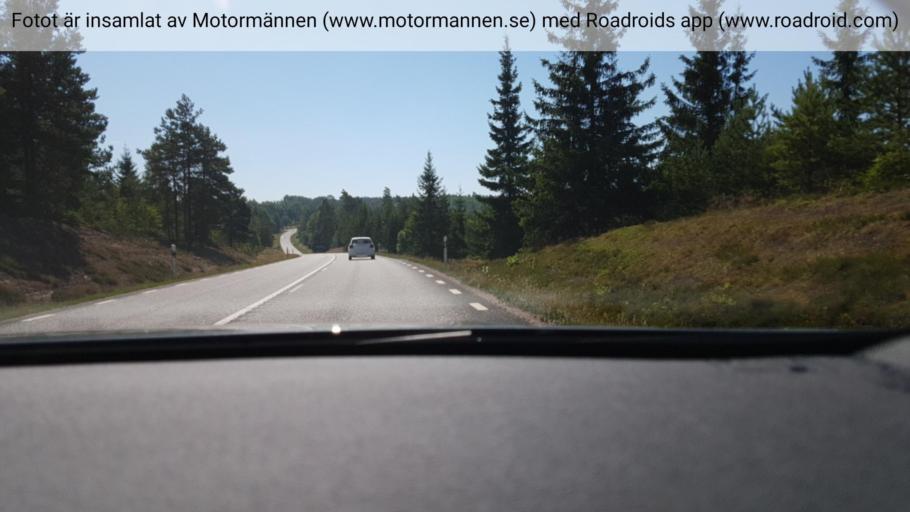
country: SE
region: Joenkoeping
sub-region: Mullsjo Kommun
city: Mullsjoe
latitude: 58.0396
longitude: 13.8284
